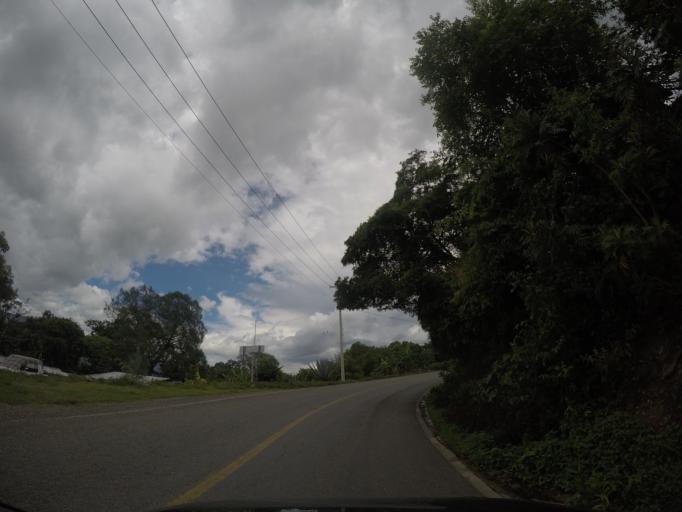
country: MX
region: Oaxaca
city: San Francisco Sola
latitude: 16.4898
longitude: -96.9847
